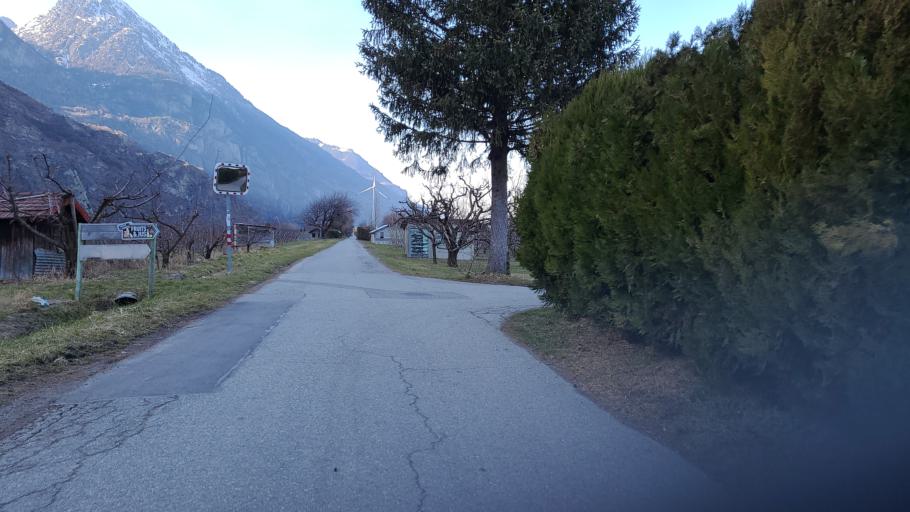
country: CH
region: Valais
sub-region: Martigny District
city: Martigny-Ville
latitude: 46.1162
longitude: 7.0621
